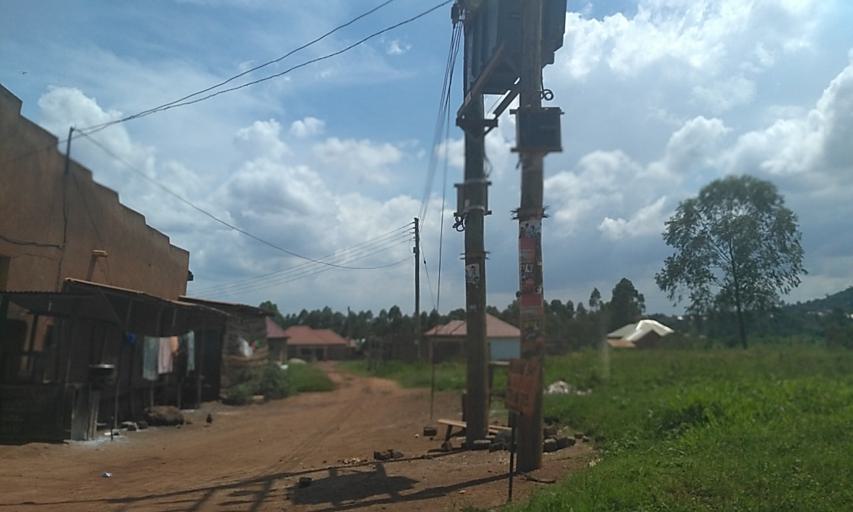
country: UG
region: Central Region
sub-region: Wakiso District
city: Wakiso
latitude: 0.4049
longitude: 32.4902
